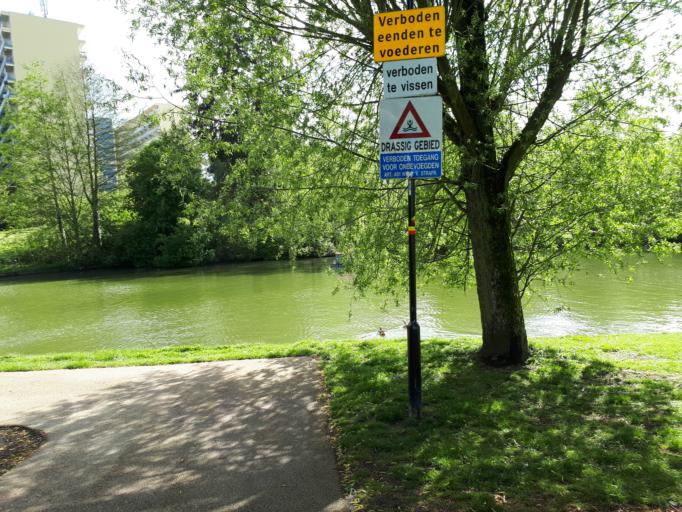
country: NL
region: Limburg
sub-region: Gemeente Vaals
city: Vaals
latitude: 50.7707
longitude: 6.0148
